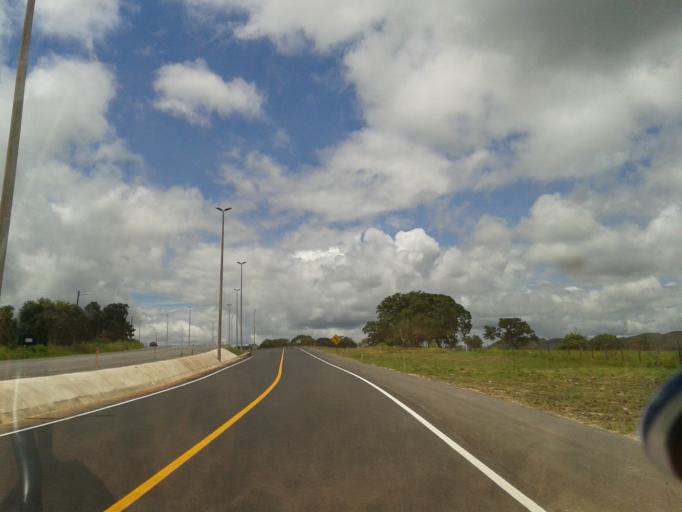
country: BR
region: Goias
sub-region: Goias
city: Goias
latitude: -15.9840
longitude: -50.0804
